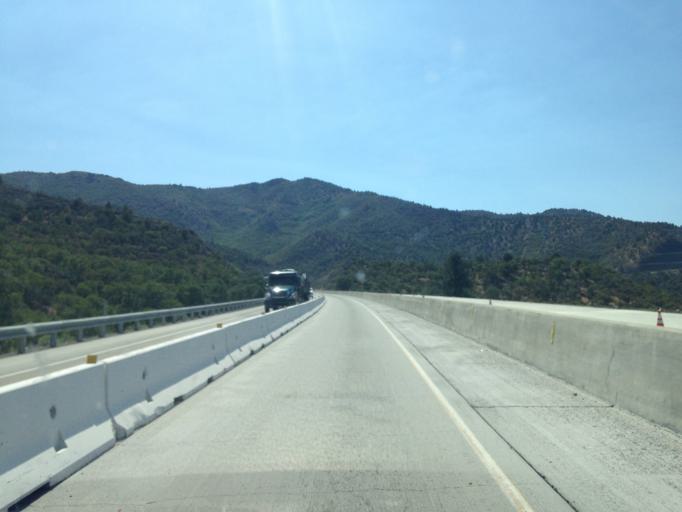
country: US
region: California
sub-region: Siskiyou County
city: Yreka
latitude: 41.8195
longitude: -122.5781
